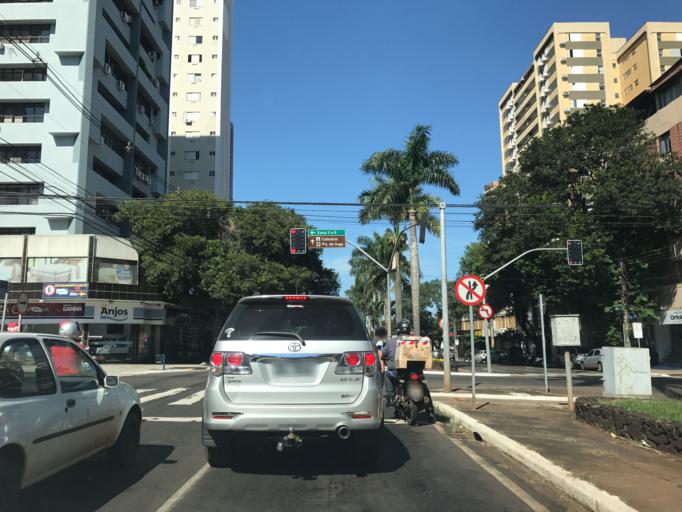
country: BR
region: Parana
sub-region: Maringa
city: Maringa
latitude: -23.4225
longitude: -51.9432
